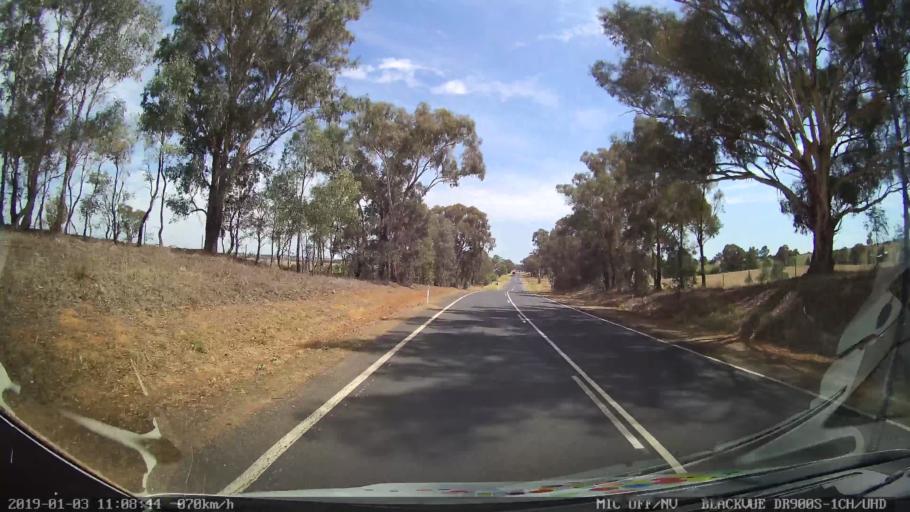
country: AU
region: New South Wales
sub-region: Young
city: Young
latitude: -34.2464
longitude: 148.2560
